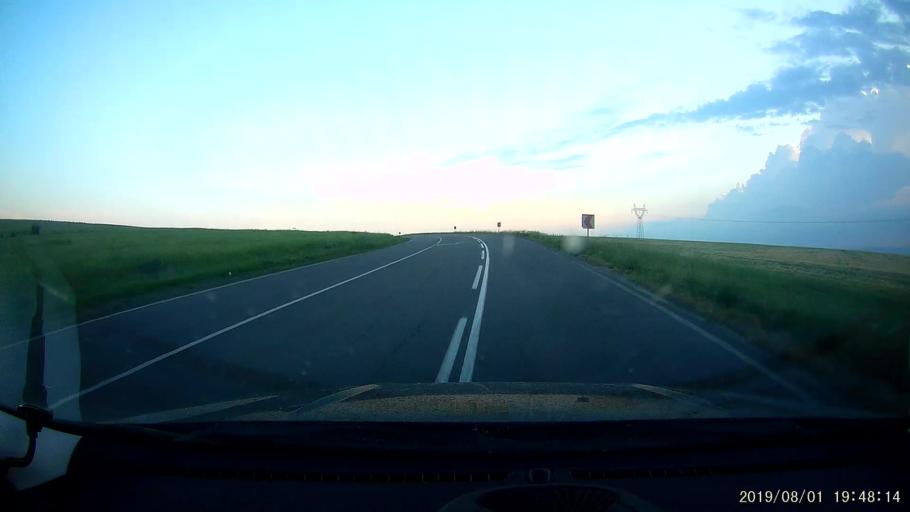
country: BG
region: Burgas
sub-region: Obshtina Karnobat
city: Karnobat
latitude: 42.6403
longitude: 26.9528
